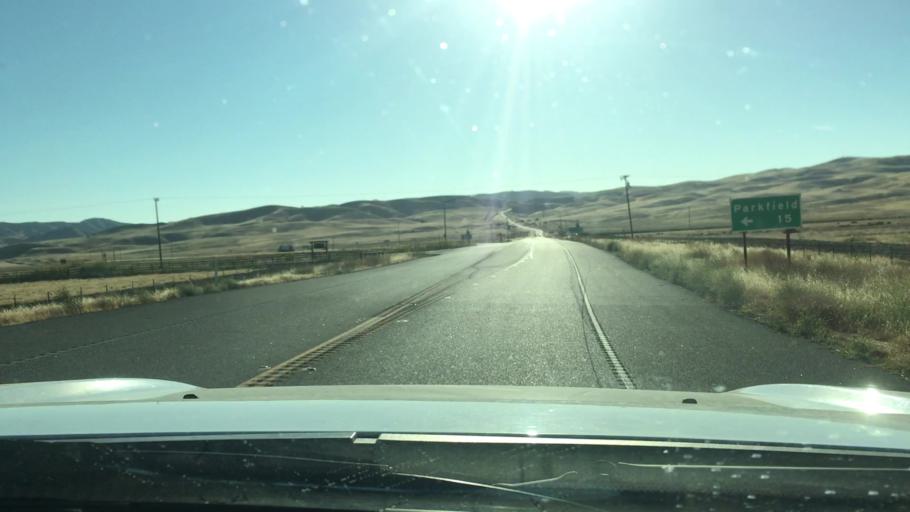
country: US
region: California
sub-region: San Luis Obispo County
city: Shandon
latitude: 35.7336
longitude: -120.2881
